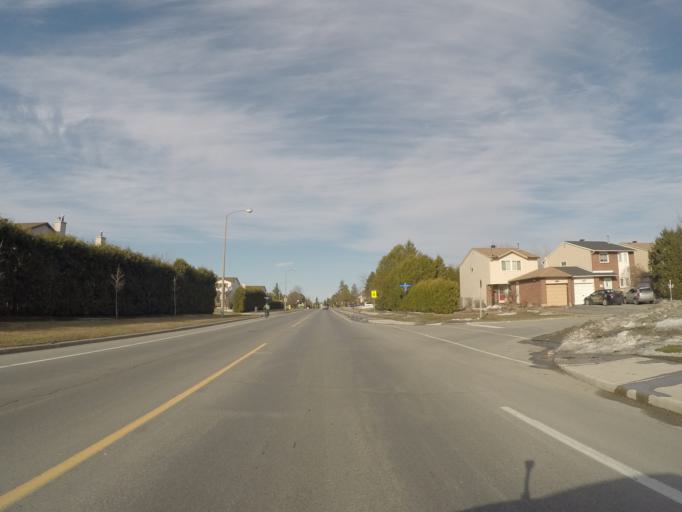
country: CA
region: Quebec
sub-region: Outaouais
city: Gatineau
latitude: 45.4645
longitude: -75.4971
